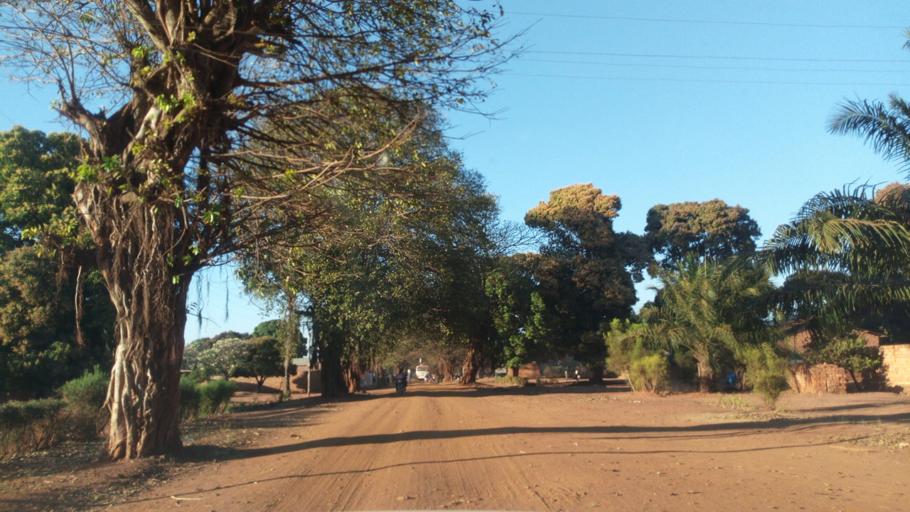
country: ZM
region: Luapula
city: Mwense
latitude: -10.3883
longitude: 28.6163
